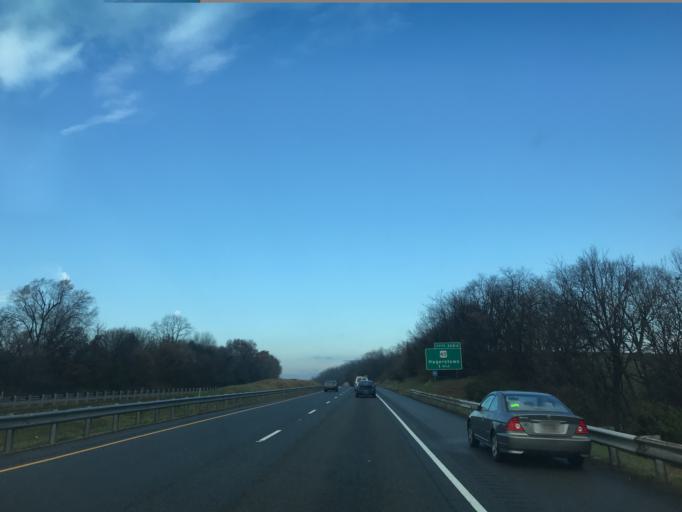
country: US
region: Maryland
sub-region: Washington County
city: Robinwood
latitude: 39.5964
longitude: -77.6575
